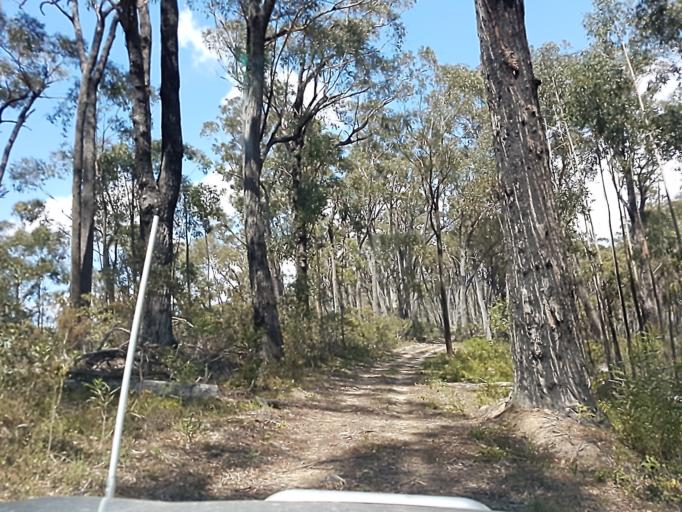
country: AU
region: Victoria
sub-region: East Gippsland
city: Lakes Entrance
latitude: -37.3129
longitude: 148.3438
